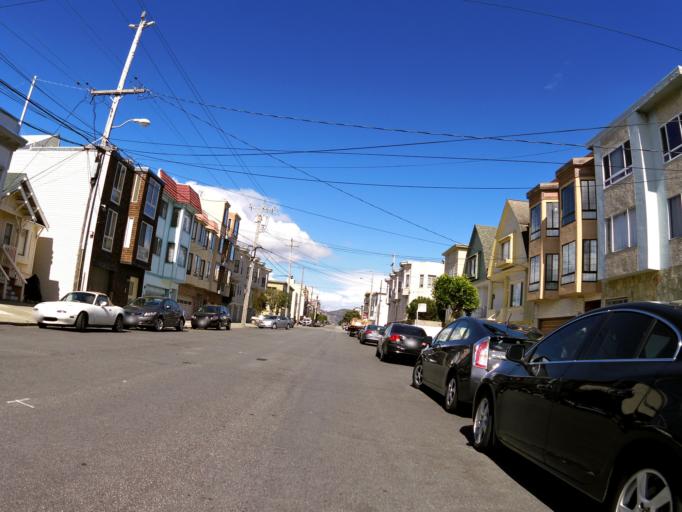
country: US
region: California
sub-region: San Francisco County
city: San Francisco
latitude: 37.7830
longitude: -122.4871
